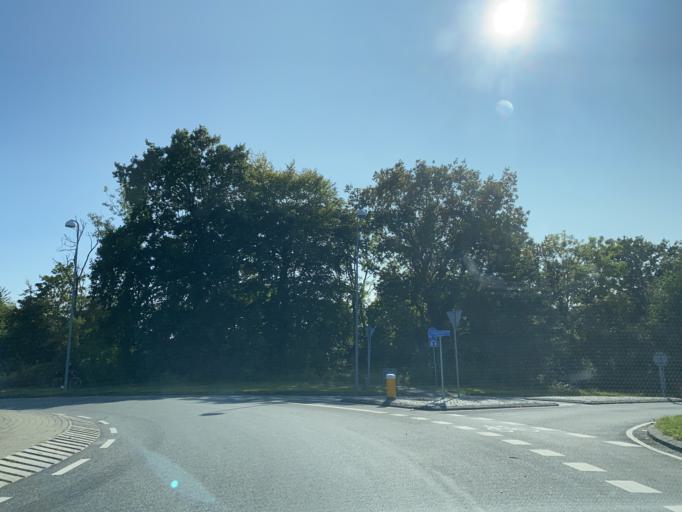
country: DK
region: South Denmark
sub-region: Aabenraa Kommune
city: Aabenraa
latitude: 55.0610
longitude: 9.3860
